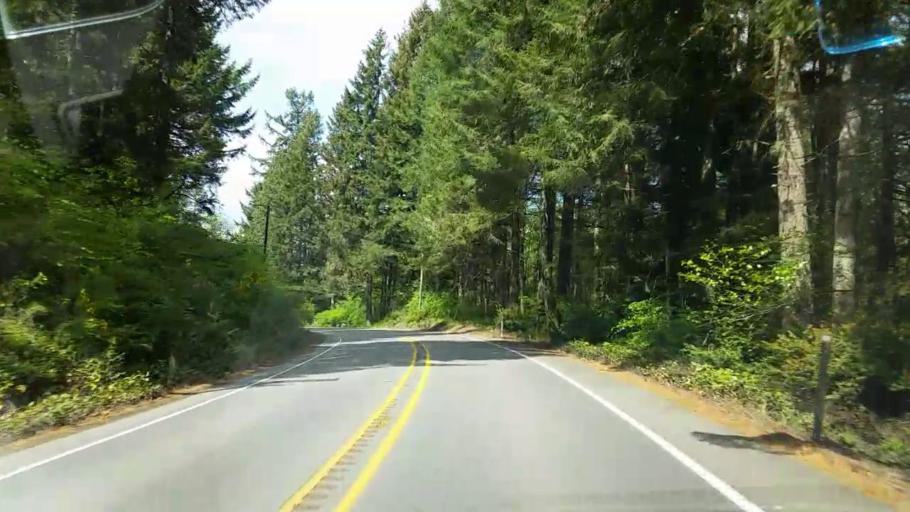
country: US
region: Washington
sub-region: Pierce County
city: Key Center
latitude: 47.3720
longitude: -122.7725
